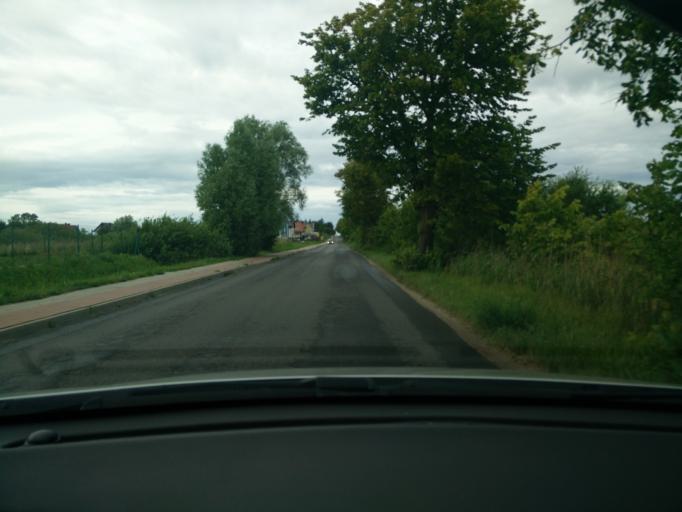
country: PL
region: Pomeranian Voivodeship
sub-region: Powiat pucki
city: Mosty
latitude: 54.6243
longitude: 18.4966
